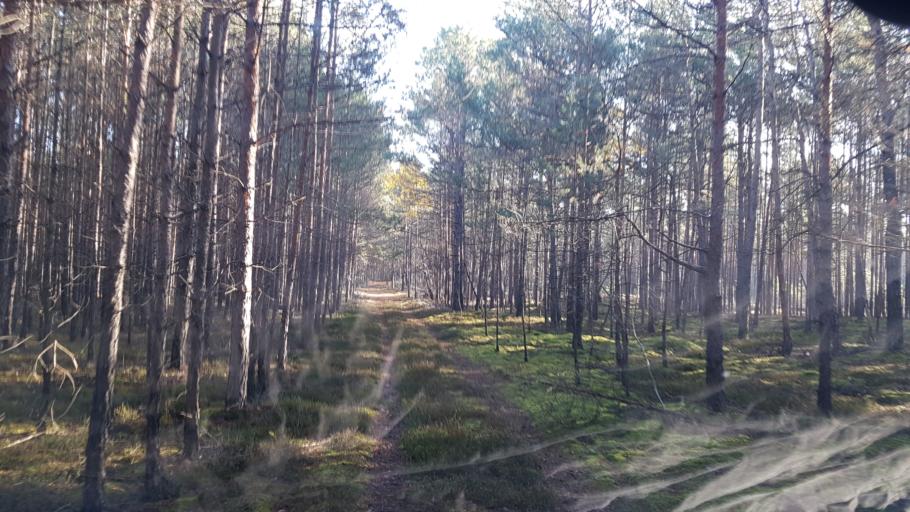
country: DE
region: Brandenburg
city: Finsterwalde
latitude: 51.6019
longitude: 13.7631
